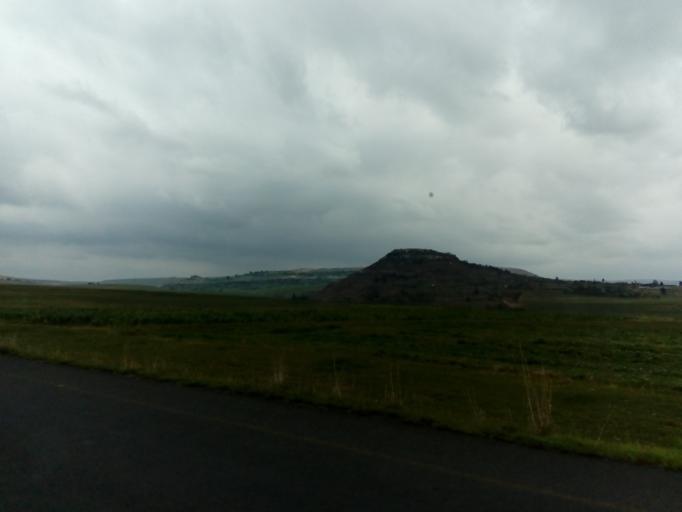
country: LS
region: Leribe
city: Leribe
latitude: -28.9859
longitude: 27.9858
